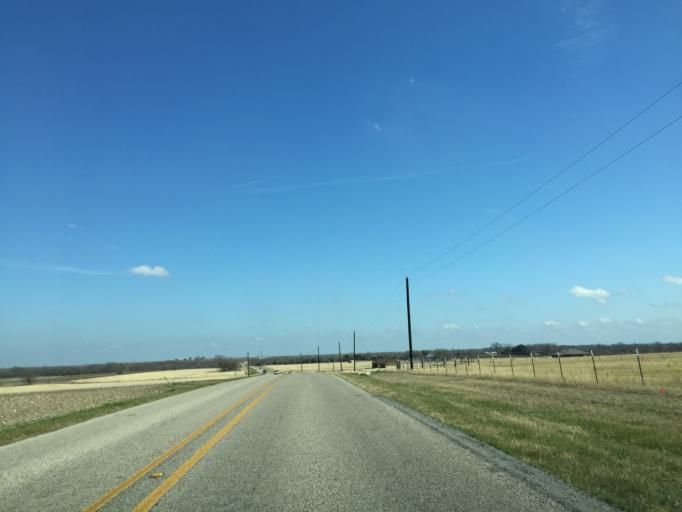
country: US
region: Texas
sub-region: Williamson County
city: Granger
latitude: 30.7538
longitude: -97.5156
